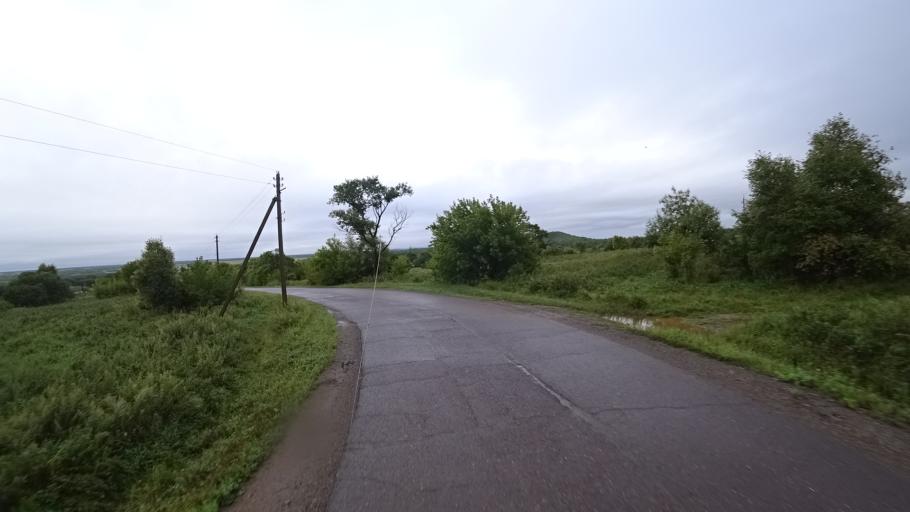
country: RU
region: Primorskiy
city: Monastyrishche
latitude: 44.2714
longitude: 132.4246
